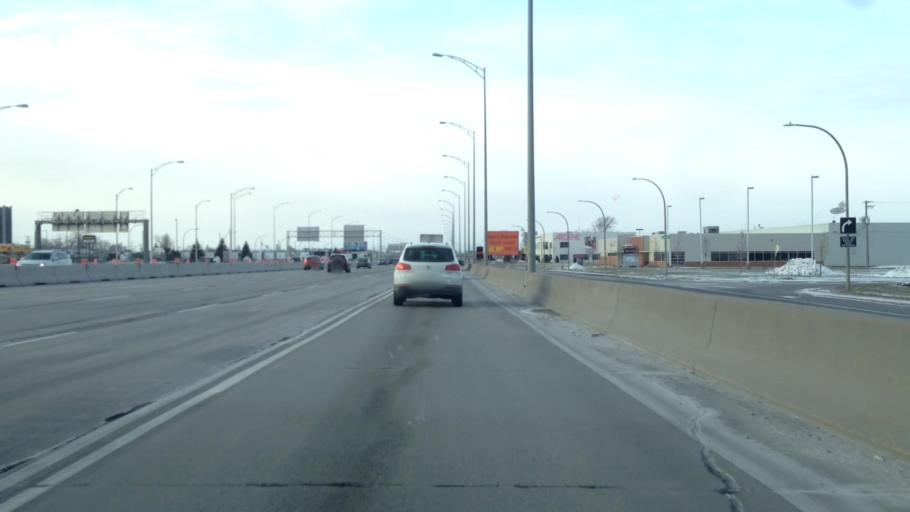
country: CA
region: Quebec
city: Dorval
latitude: 45.4931
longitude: -73.7400
